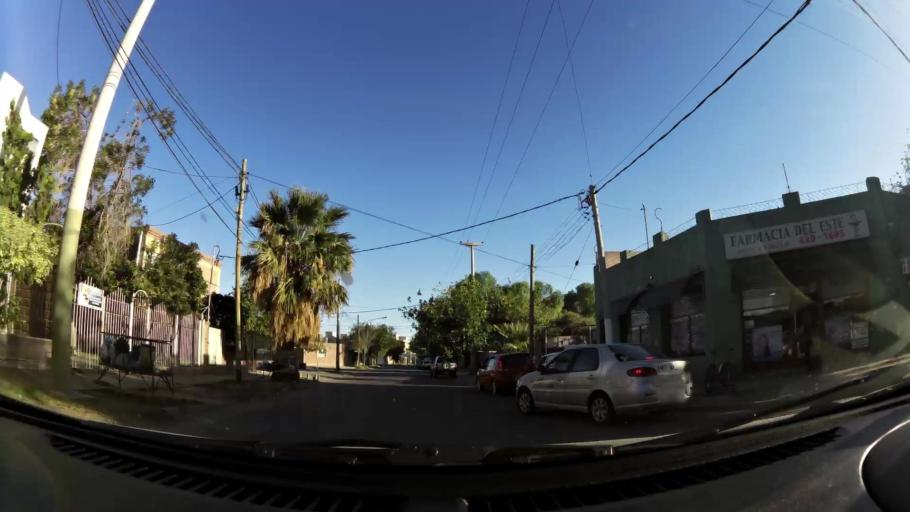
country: AR
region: San Juan
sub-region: Departamento de Santa Lucia
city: Santa Lucia
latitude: -31.5500
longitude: -68.5129
